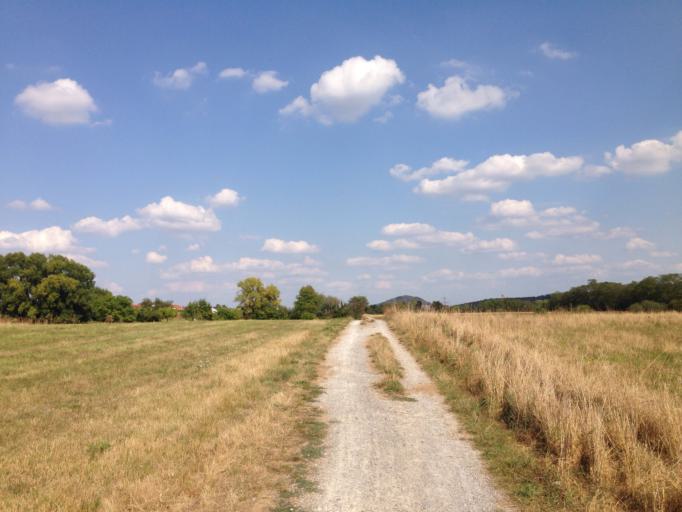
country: DE
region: Hesse
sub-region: Regierungsbezirk Giessen
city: Giessen
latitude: 50.6249
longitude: 8.6635
